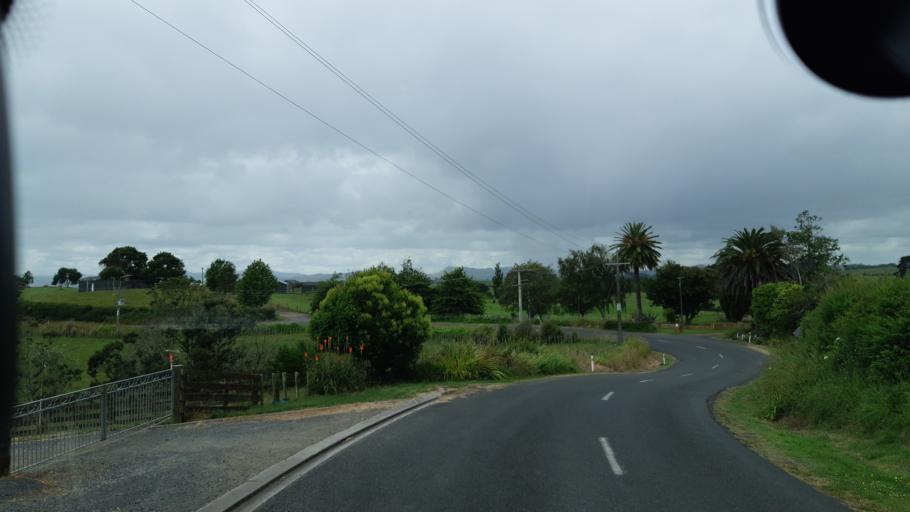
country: NZ
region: Waikato
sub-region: Waikato District
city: Te Kauwhata
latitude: -37.5130
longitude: 175.0839
